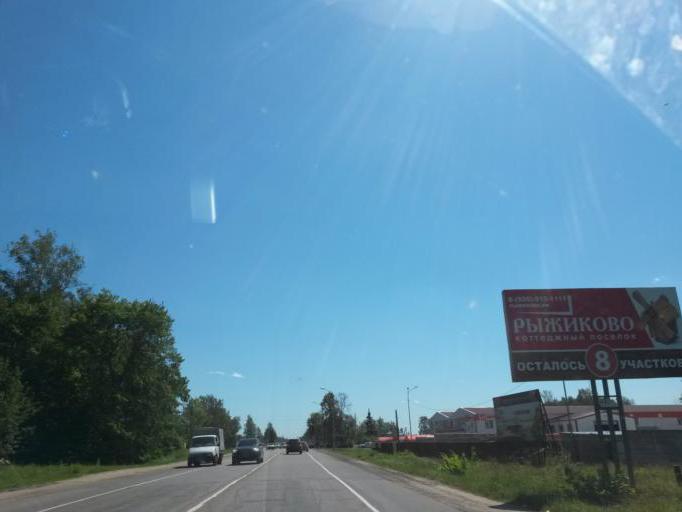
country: RU
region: Moskovskaya
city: Proletarskiy
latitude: 55.0326
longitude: 37.4285
